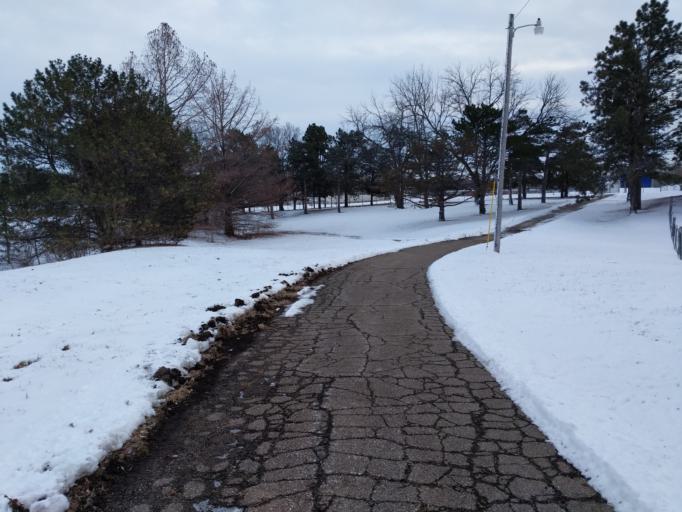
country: US
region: Kansas
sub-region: Riley County
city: Manhattan
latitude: 39.2019
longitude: -96.6202
